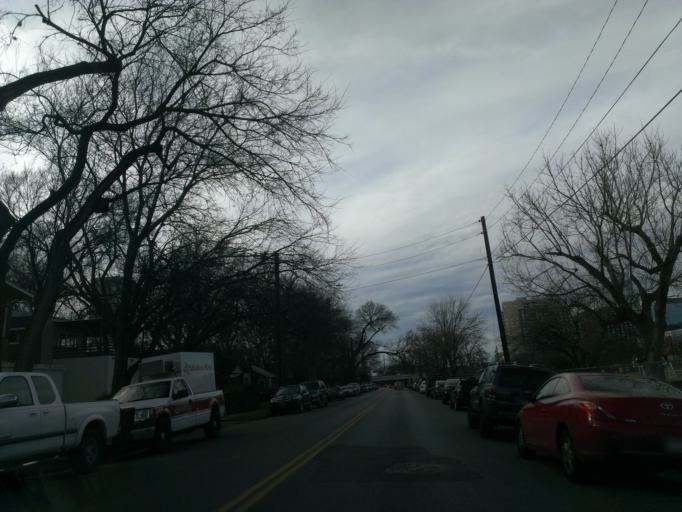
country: US
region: Texas
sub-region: Travis County
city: Austin
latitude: 30.2565
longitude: -97.7344
